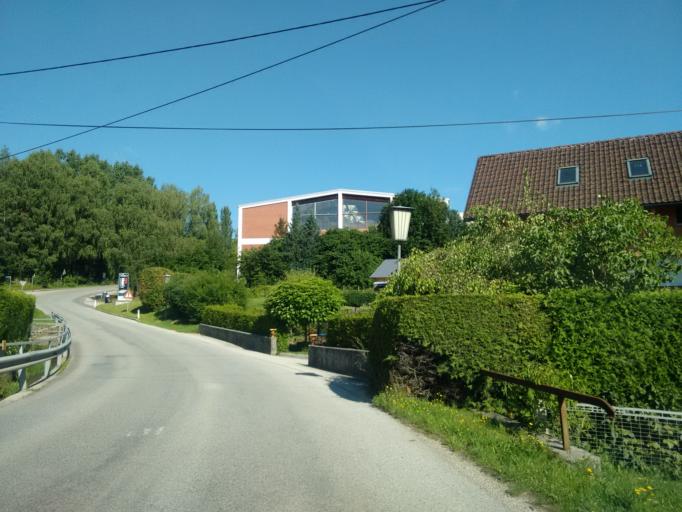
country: AT
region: Upper Austria
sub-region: Politischer Bezirk Steyr-Land
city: Pfarrkirchen bei Bad Hall
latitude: 48.0245
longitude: 14.2064
